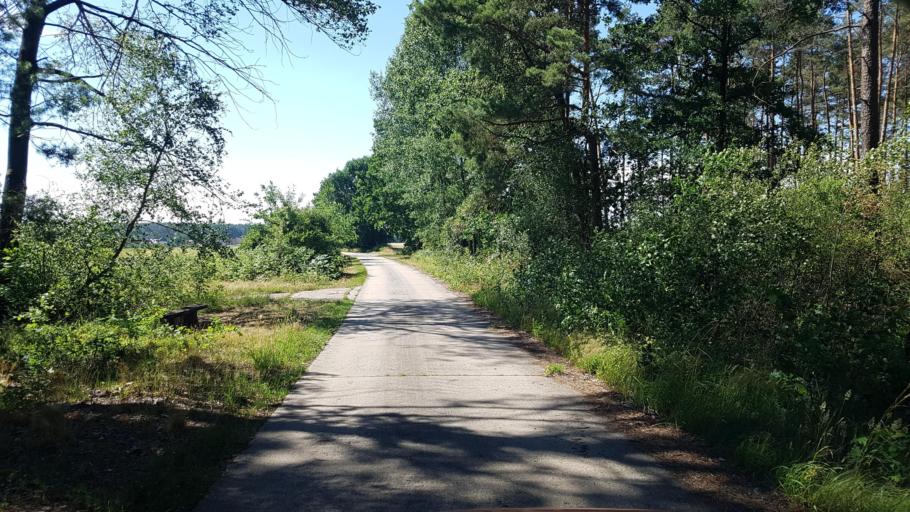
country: DE
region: Brandenburg
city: Bronkow
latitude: 51.6943
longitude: 13.9471
